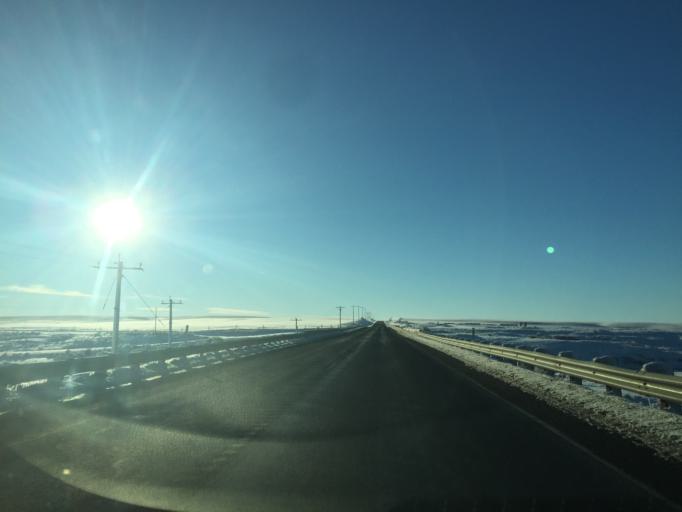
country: US
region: Washington
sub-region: Okanogan County
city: Coulee Dam
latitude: 47.7396
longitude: -118.8423
